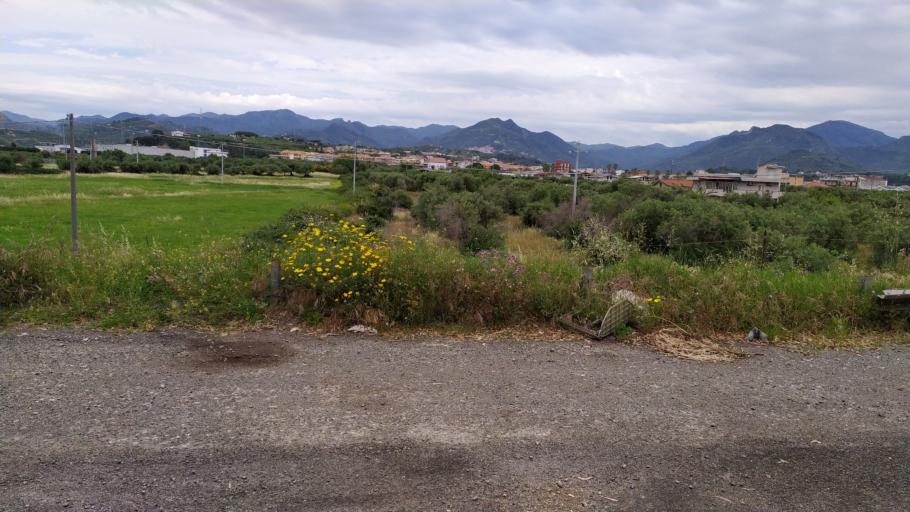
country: IT
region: Sicily
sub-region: Messina
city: San Filippo del Mela
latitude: 38.1848
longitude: 15.2609
